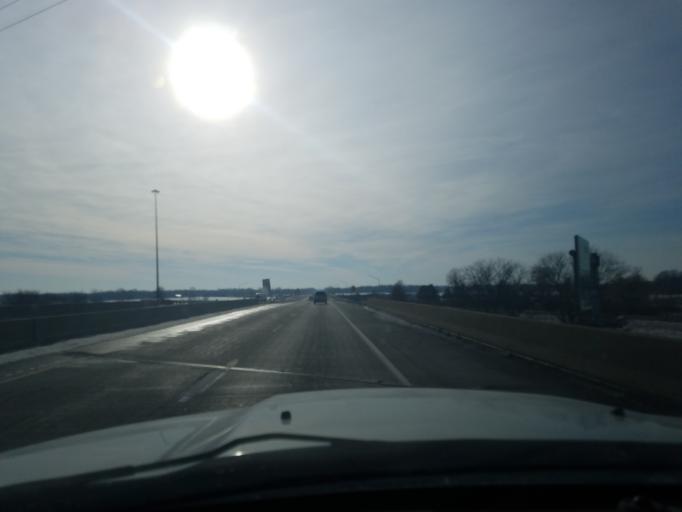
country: US
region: Indiana
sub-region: Huntington County
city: Warren
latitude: 40.7203
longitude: -85.4366
